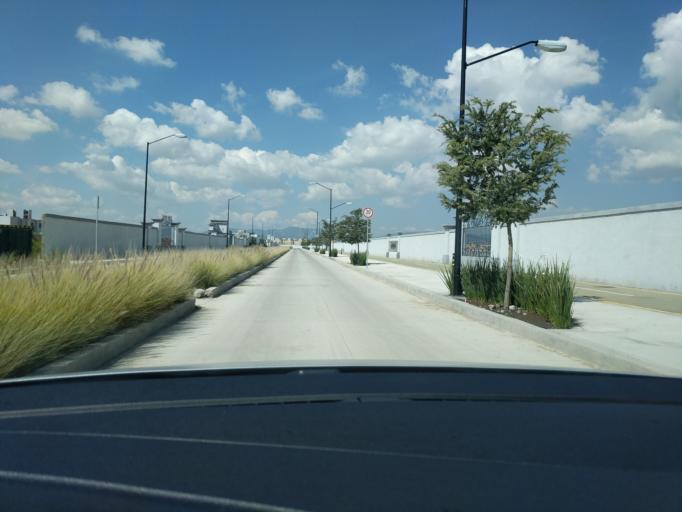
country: MX
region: Hidalgo
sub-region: Zempoala
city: Lindavista
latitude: 20.0067
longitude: -98.7787
